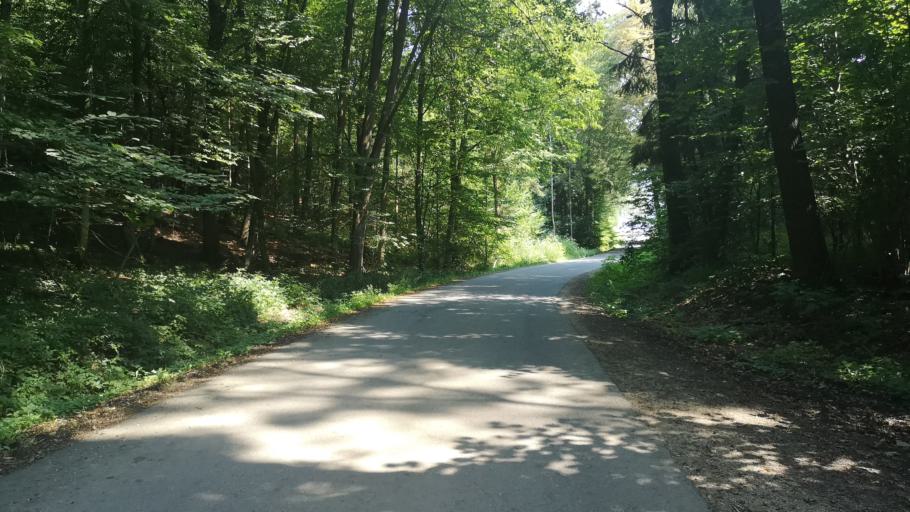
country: AT
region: Styria
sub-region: Politischer Bezirk Deutschlandsberg
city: Lannach
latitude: 46.9340
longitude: 15.3468
